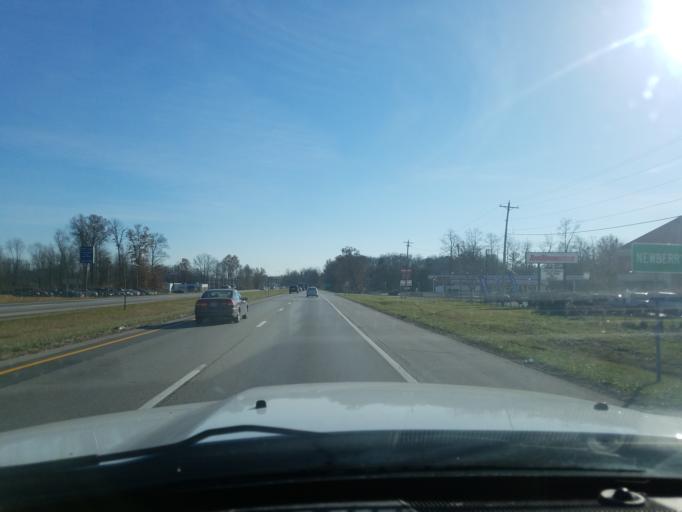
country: US
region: Ohio
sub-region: Clermont County
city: Summerside
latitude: 39.0904
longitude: -84.2470
